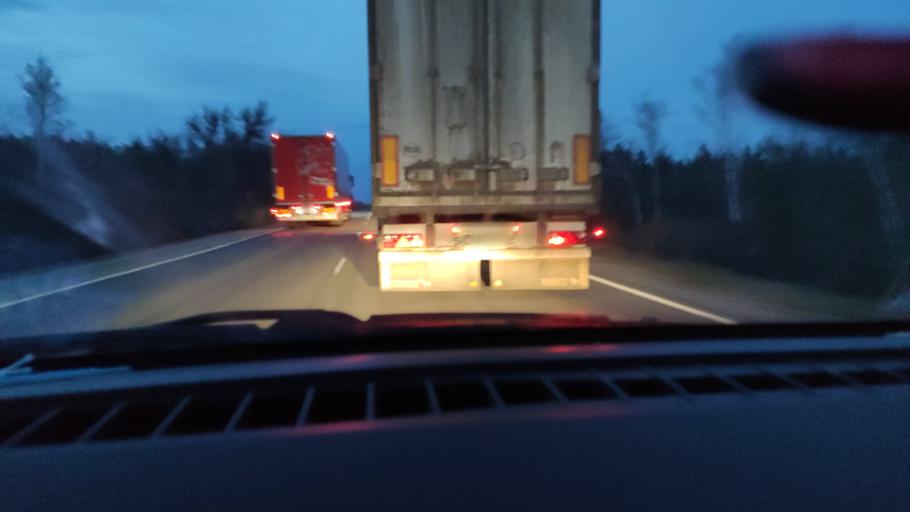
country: RU
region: Saratov
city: Sennoy
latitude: 52.1171
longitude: 46.8397
